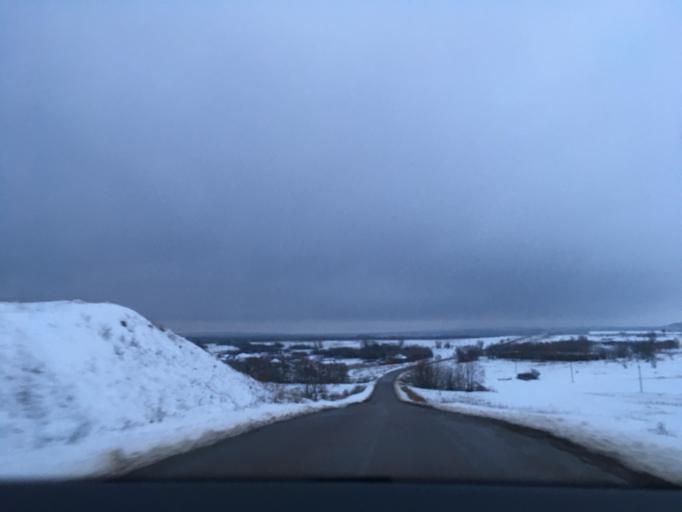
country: RU
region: Voronezj
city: Verkhniy Mamon
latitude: 50.0714
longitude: 40.3144
